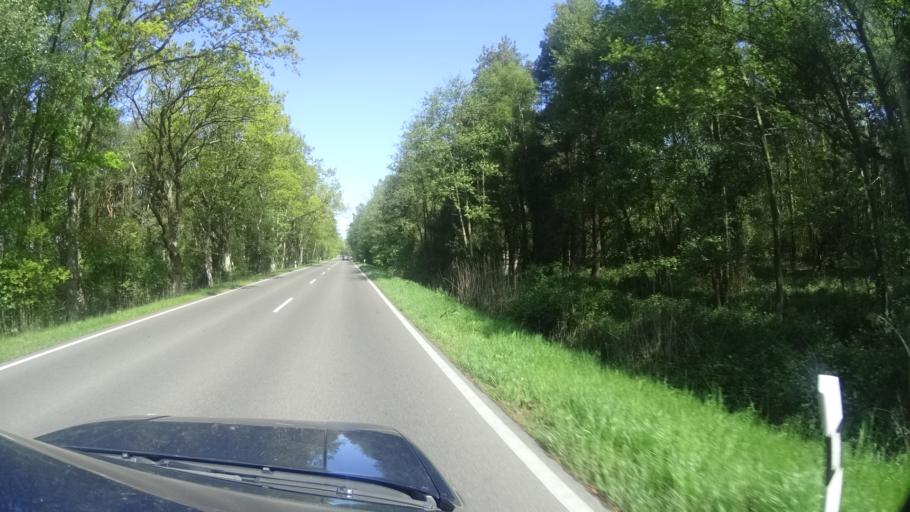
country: DE
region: Mecklenburg-Vorpommern
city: Zingst
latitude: 54.4377
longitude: 12.6498
